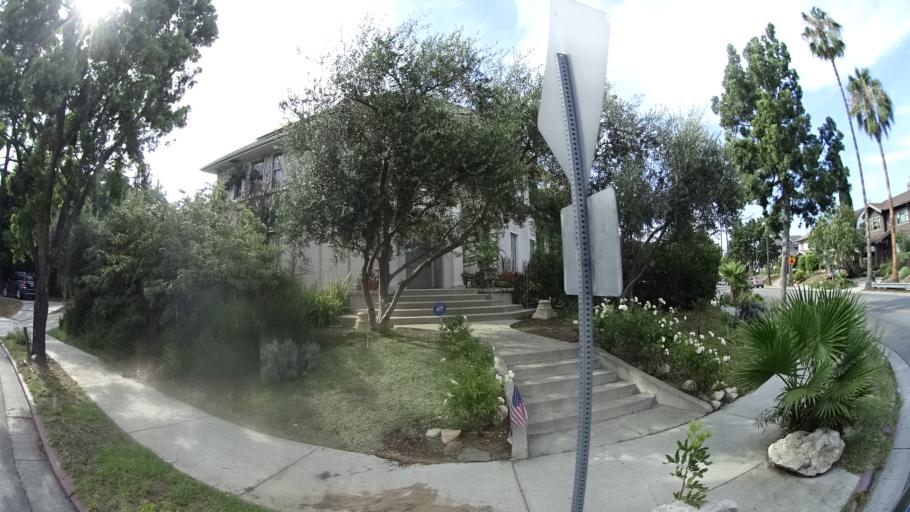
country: US
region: California
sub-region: Los Angeles County
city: Hollywood
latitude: 34.0718
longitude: -118.3135
